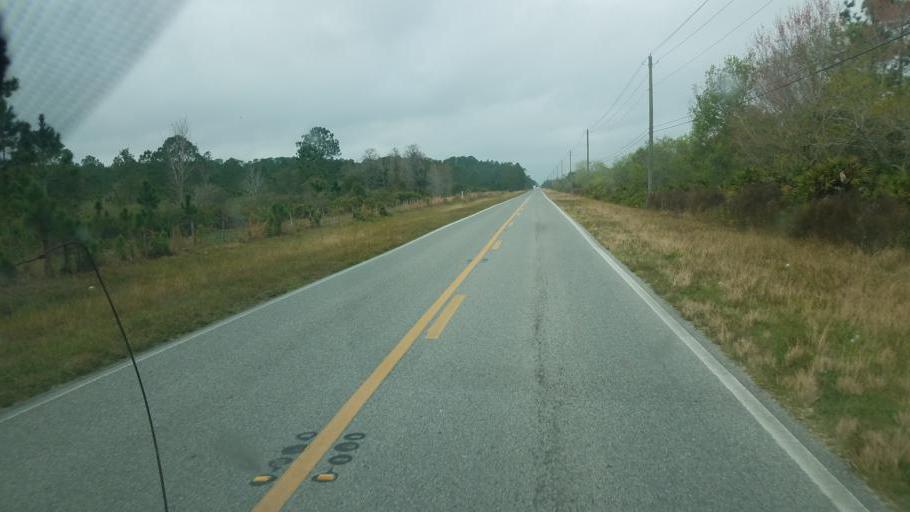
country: US
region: Florida
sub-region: Polk County
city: Polk City
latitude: 28.2591
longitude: -81.8798
